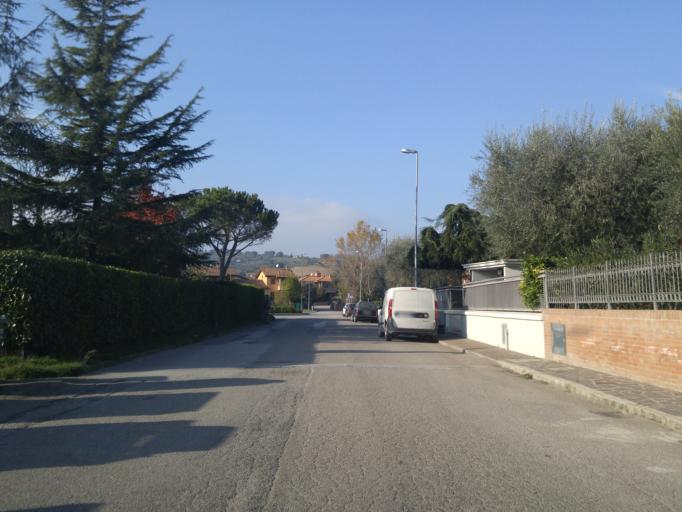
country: IT
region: The Marches
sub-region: Provincia di Pesaro e Urbino
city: Calcinelli
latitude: 43.7559
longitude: 12.9203
